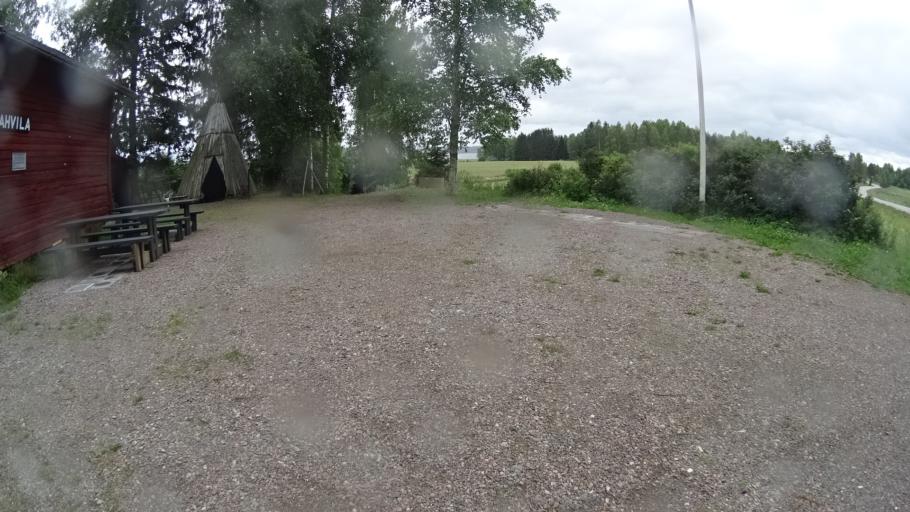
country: FI
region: Uusimaa
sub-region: Helsinki
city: Karkkila
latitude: 60.5836
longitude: 24.3423
